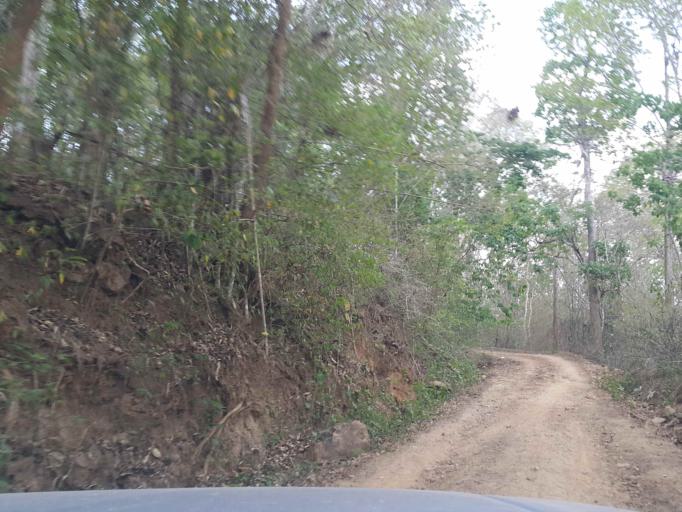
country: TH
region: Chiang Mai
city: Wiang Haeng
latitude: 19.3670
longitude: 98.7174
